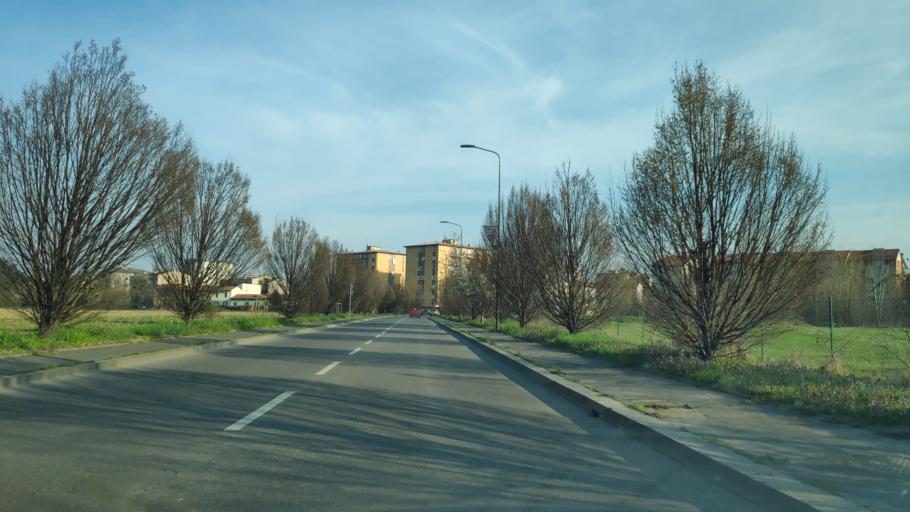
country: IT
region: Lombardy
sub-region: Citta metropolitana di Milano
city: Figino
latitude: 45.4691
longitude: 9.0822
